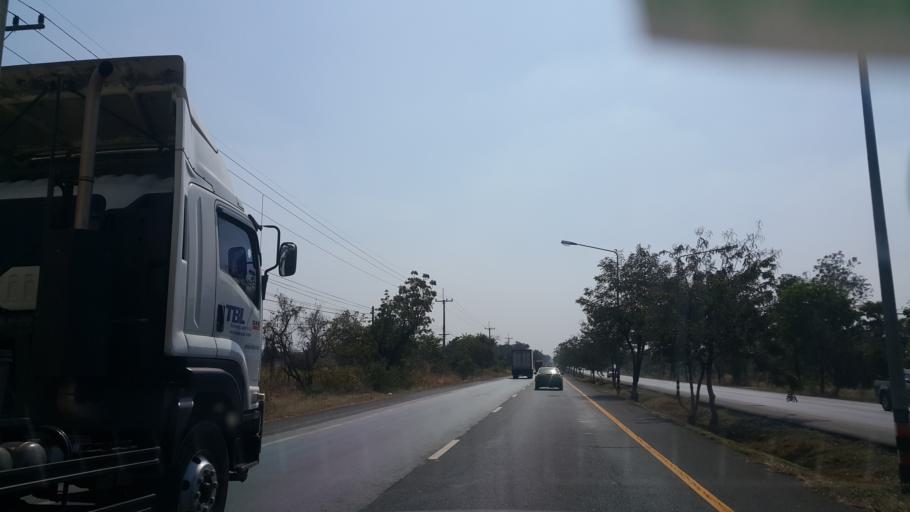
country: TH
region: Nakhon Ratchasima
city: Non Daeng
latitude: 15.3750
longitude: 102.4596
